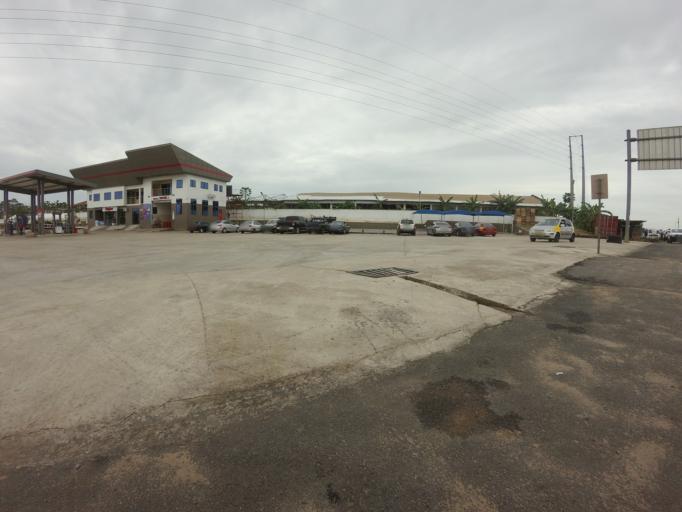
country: GH
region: Eastern
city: Nsawam
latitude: 5.7911
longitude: -0.3384
